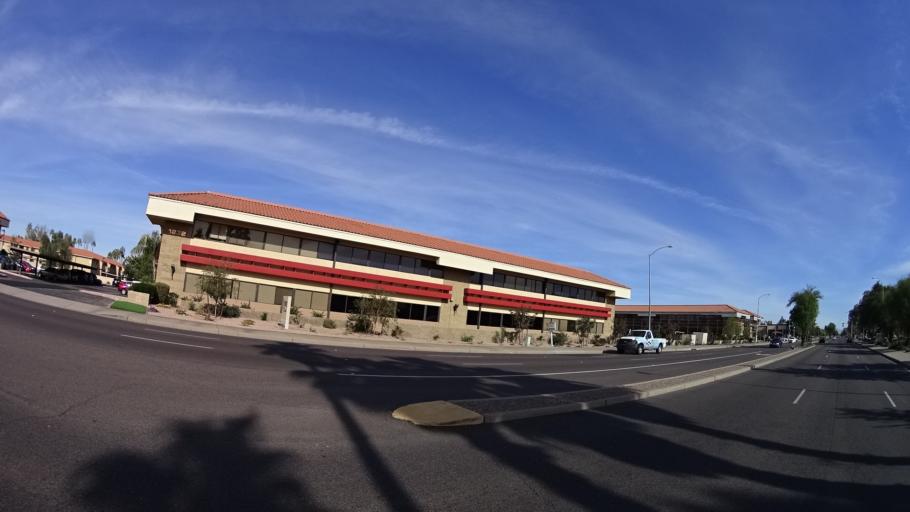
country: US
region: Arizona
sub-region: Maricopa County
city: Tempe
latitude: 33.4075
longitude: -111.9194
